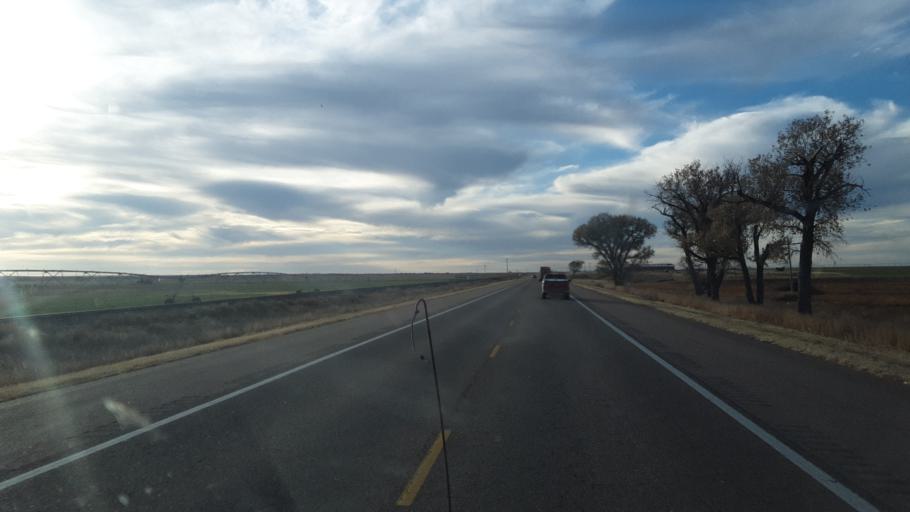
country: US
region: Kansas
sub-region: Hamilton County
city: Syracuse
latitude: 37.9532
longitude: -101.6263
